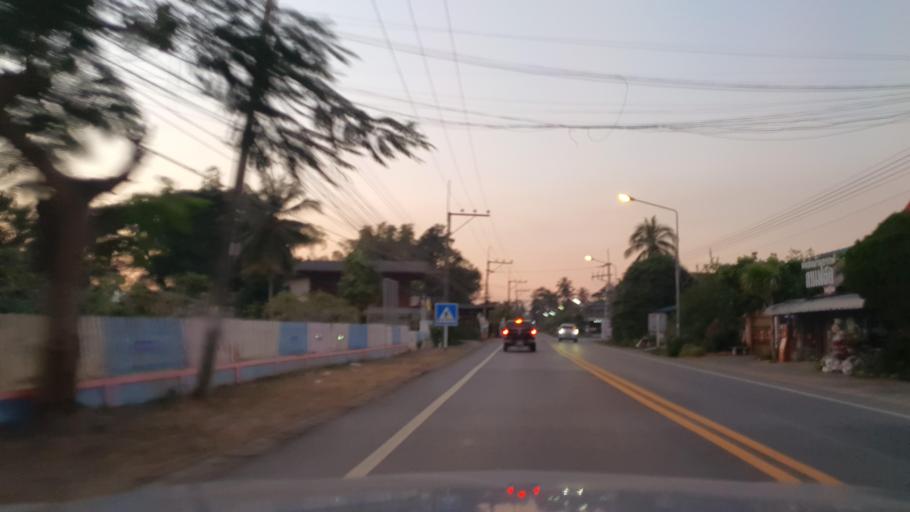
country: TH
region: Phayao
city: Dok Kham Tai
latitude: 19.1408
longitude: 100.0163
